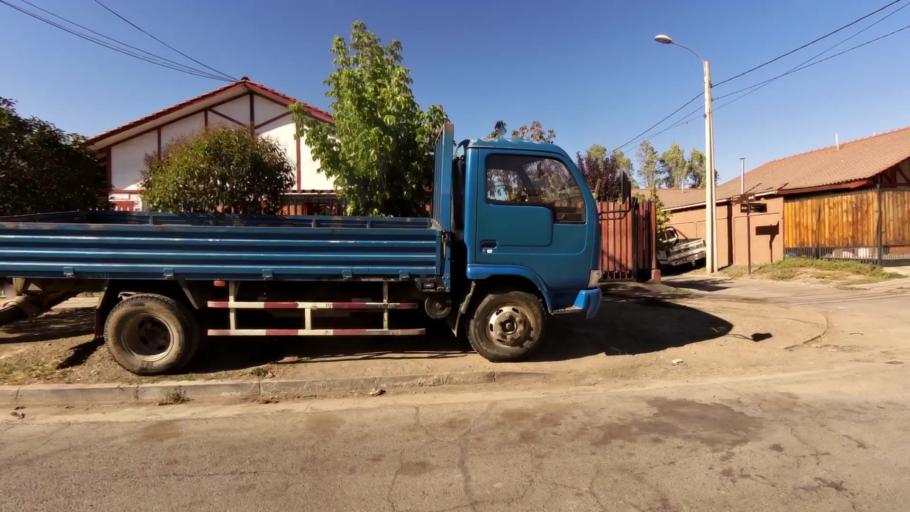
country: CL
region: O'Higgins
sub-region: Provincia de Cachapoal
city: Rancagua
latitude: -34.1799
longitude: -70.7622
